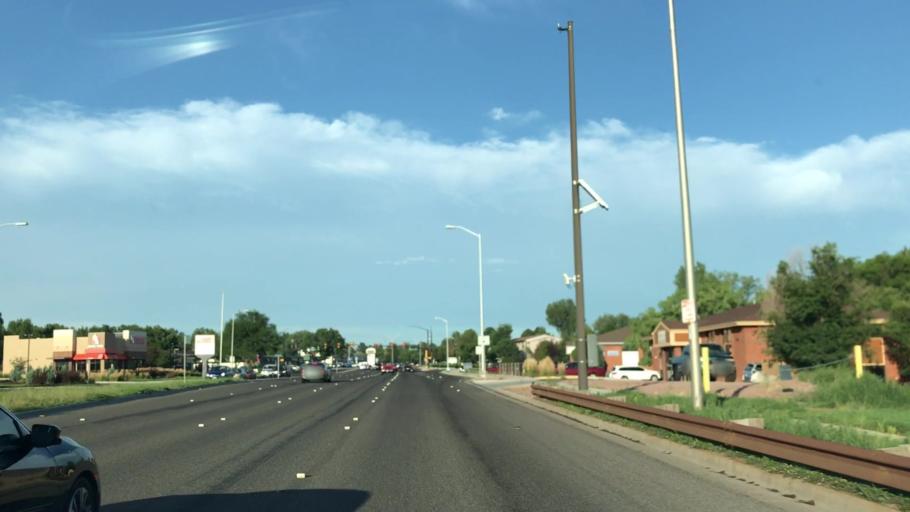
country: US
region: Colorado
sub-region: El Paso County
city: Colorado Springs
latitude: 38.8899
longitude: -104.7693
